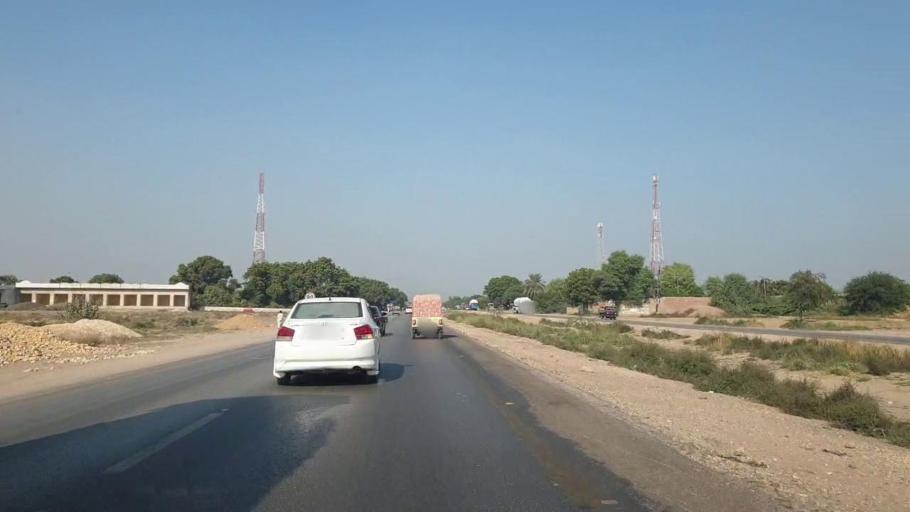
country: PK
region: Sindh
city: Matiari
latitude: 25.5007
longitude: 68.4250
